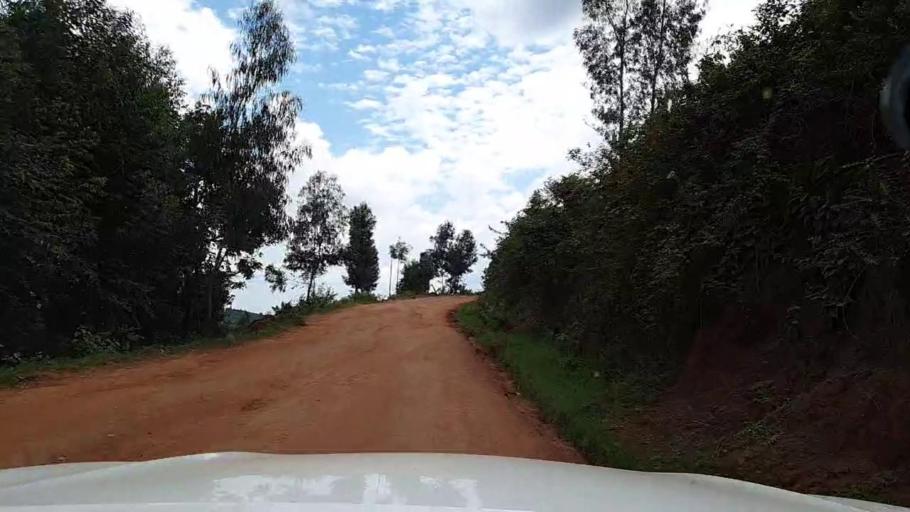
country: RW
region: Southern Province
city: Butare
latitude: -2.7096
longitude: 29.5410
